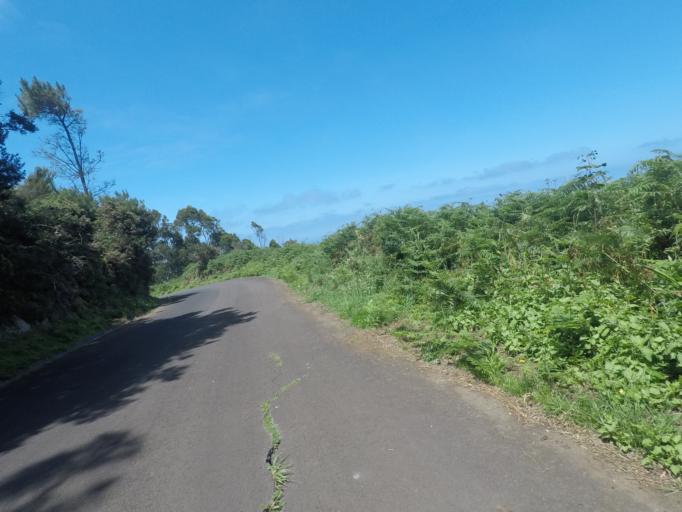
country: PT
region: Madeira
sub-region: Porto Moniz
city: Porto Moniz
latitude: 32.8441
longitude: -17.1504
